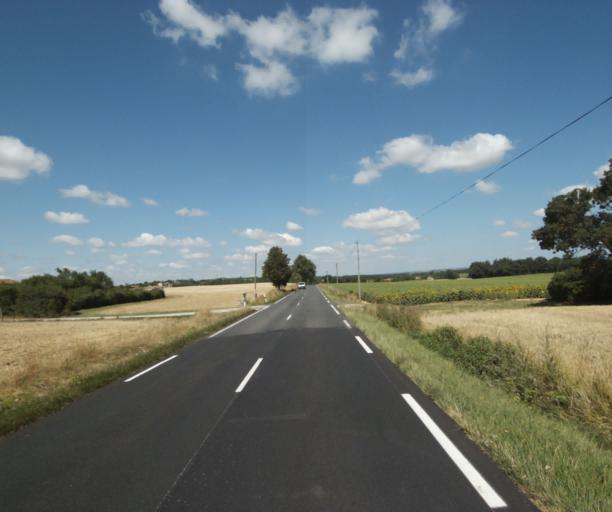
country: FR
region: Midi-Pyrenees
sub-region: Departement de la Haute-Garonne
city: Auriac-sur-Vendinelle
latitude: 43.4655
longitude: 1.8082
